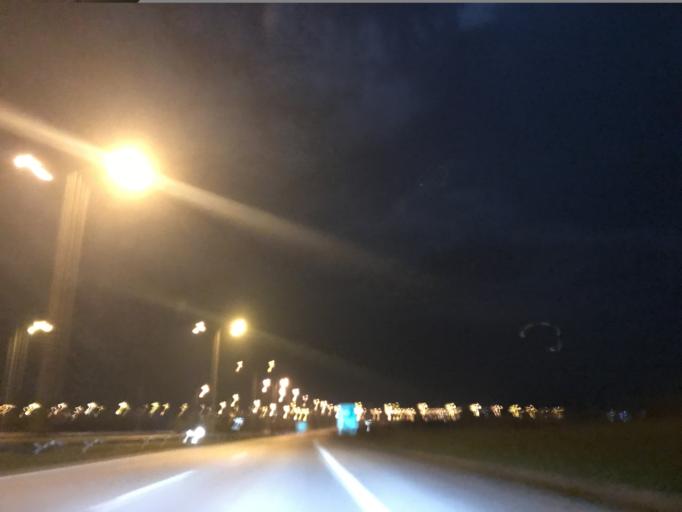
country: TR
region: Hatay
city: Mahmutlar
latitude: 36.9649
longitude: 36.1036
